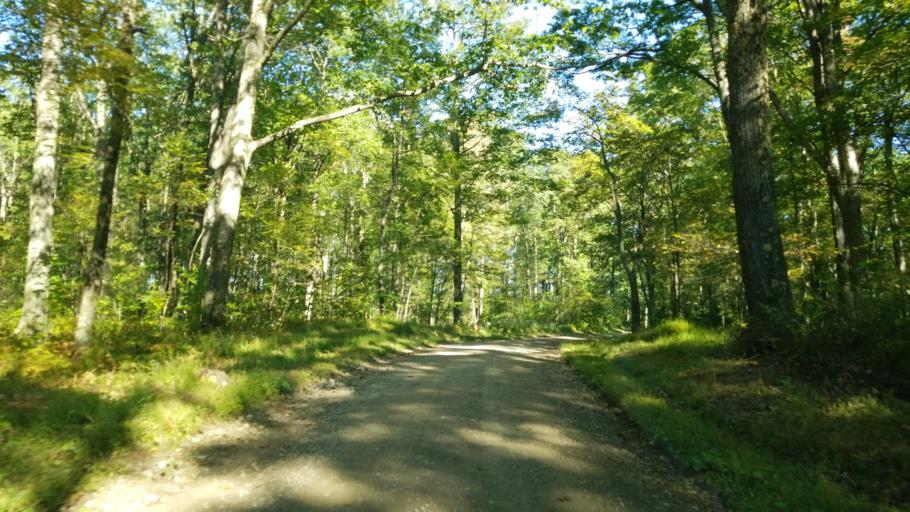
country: US
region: Pennsylvania
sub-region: Clearfield County
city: Curwensville
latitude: 41.1150
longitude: -78.5722
